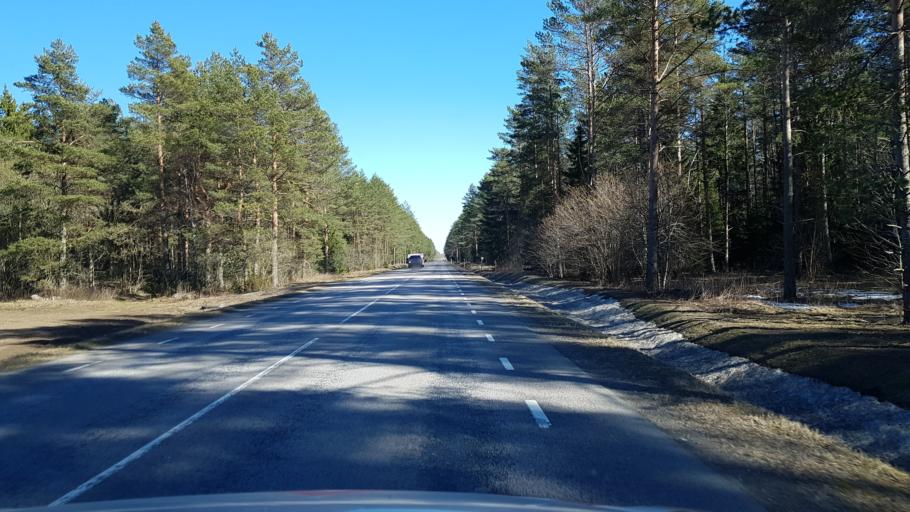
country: EE
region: Laeaene-Virumaa
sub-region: Viru-Nigula vald
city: Kunda
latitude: 59.3603
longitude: 26.6273
